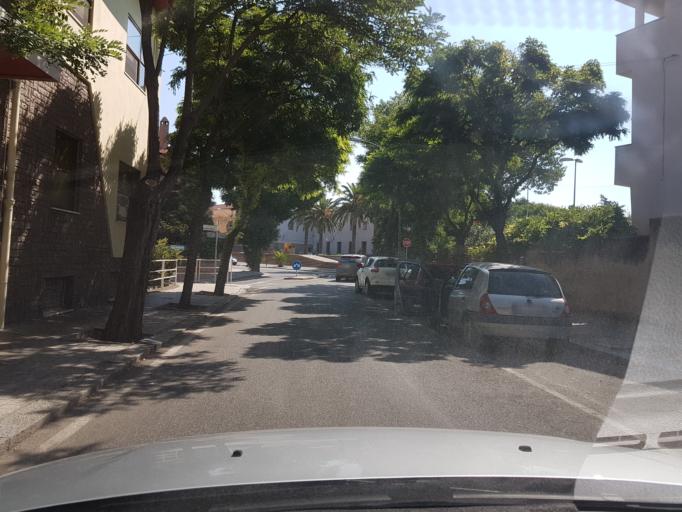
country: IT
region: Sardinia
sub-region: Provincia di Oristano
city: Oristano
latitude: 39.8997
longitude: 8.5901
